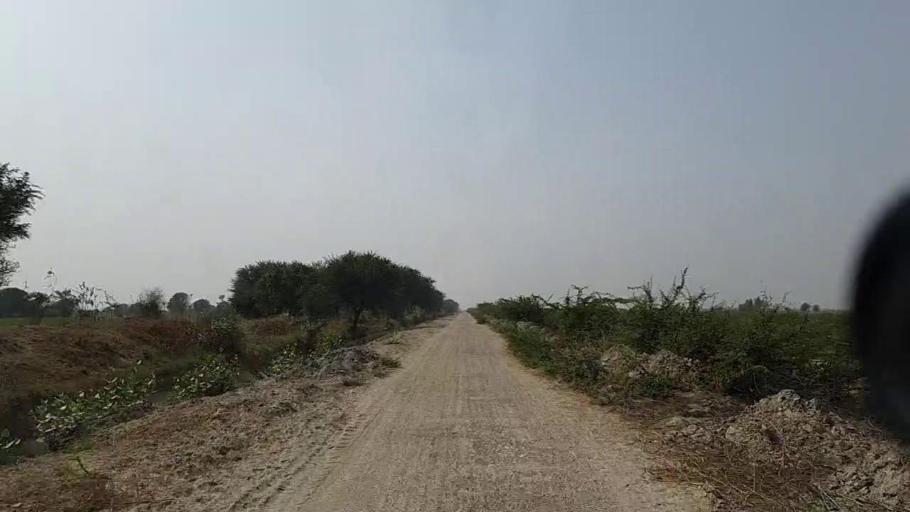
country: PK
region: Sindh
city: Naukot
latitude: 24.7701
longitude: 69.3378
